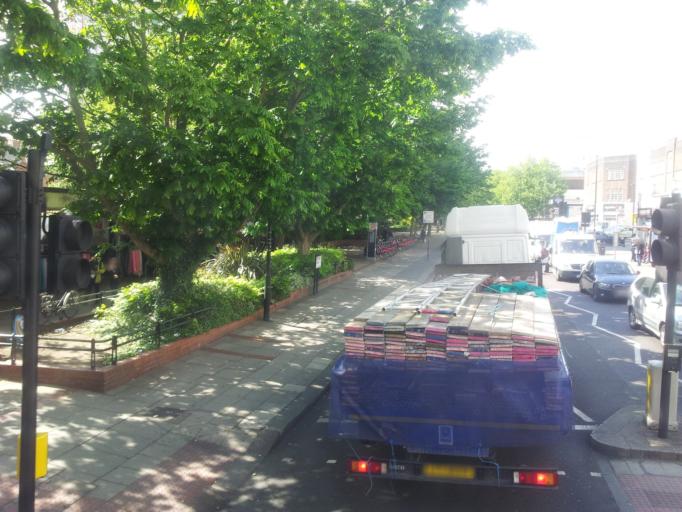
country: GB
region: England
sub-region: Greater London
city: Bayswater
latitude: 51.5231
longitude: -0.1747
